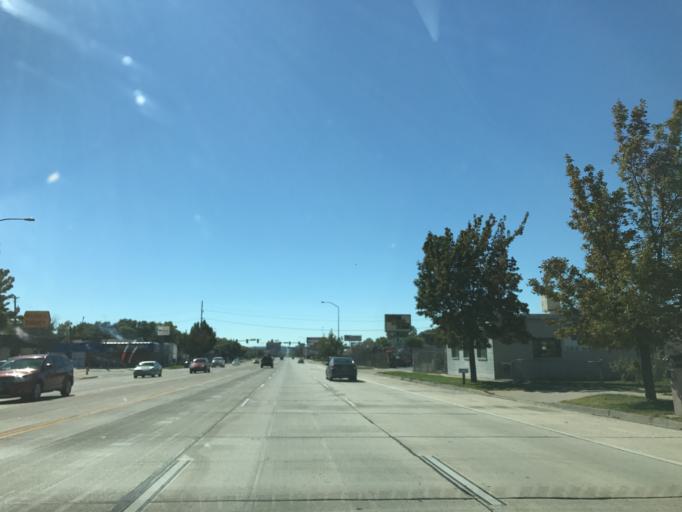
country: US
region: Utah
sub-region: Weber County
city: Ogden
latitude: 41.2386
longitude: -111.9702
